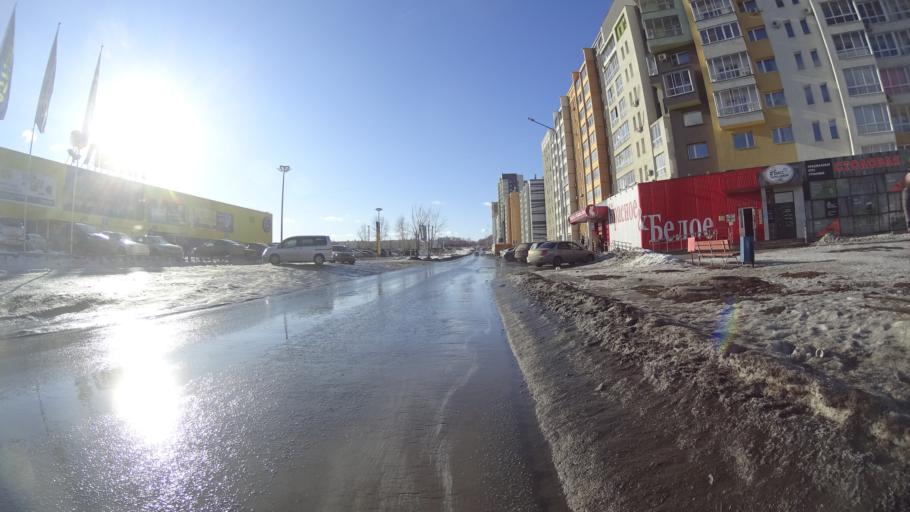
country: RU
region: Chelyabinsk
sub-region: Gorod Chelyabinsk
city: Chelyabinsk
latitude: 55.1599
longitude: 61.2942
